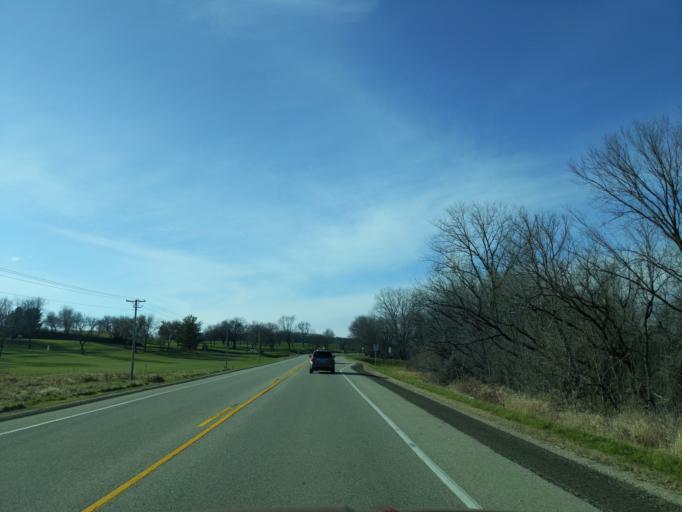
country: US
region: Wisconsin
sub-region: Rock County
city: Edgerton
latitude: 42.8271
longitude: -89.0132
